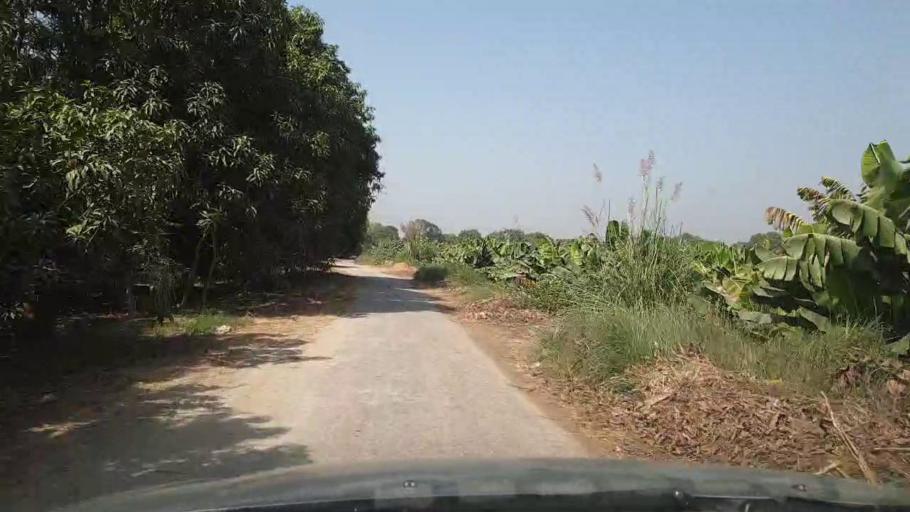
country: PK
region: Sindh
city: Tando Jam
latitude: 25.3614
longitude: 68.5203
